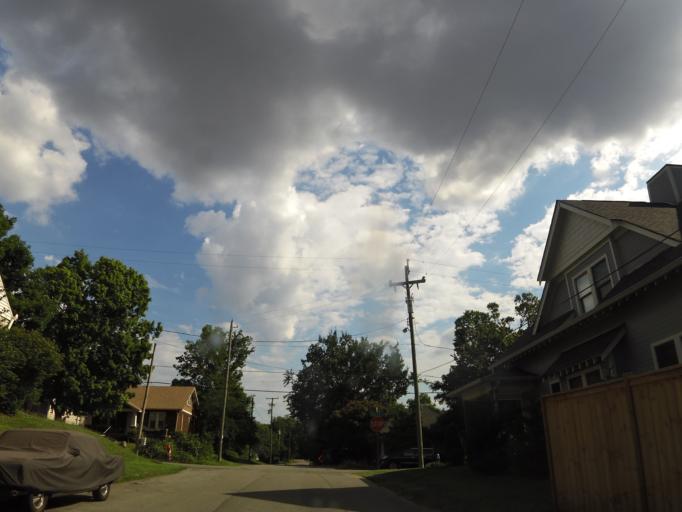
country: US
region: Tennessee
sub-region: Davidson County
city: Nashville
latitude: 36.1760
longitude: -86.7442
